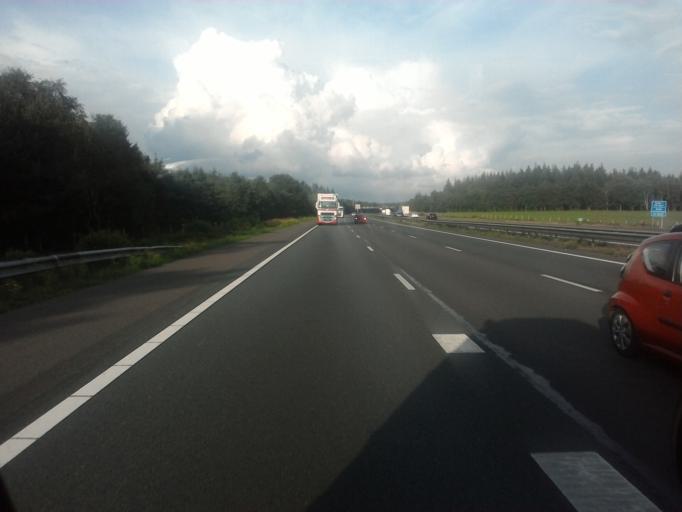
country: NL
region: Gelderland
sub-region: Gemeente Renkum
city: Oosterbeek
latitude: 52.0281
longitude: 5.8378
